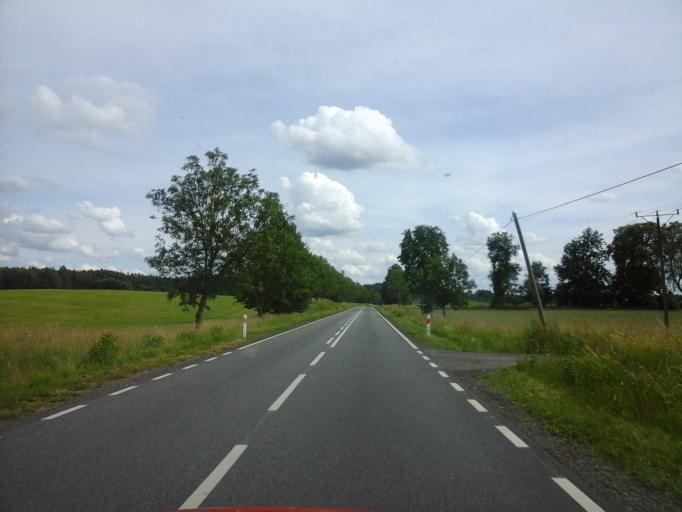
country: PL
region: West Pomeranian Voivodeship
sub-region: Powiat lobeski
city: Wegorzyno
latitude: 53.5228
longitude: 15.5675
